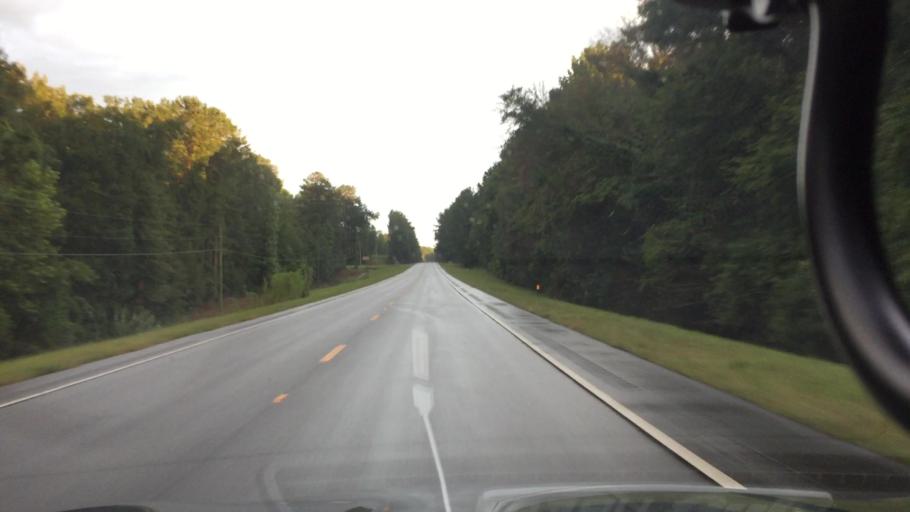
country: US
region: Alabama
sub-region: Coffee County
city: New Brockton
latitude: 31.5639
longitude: -85.9251
